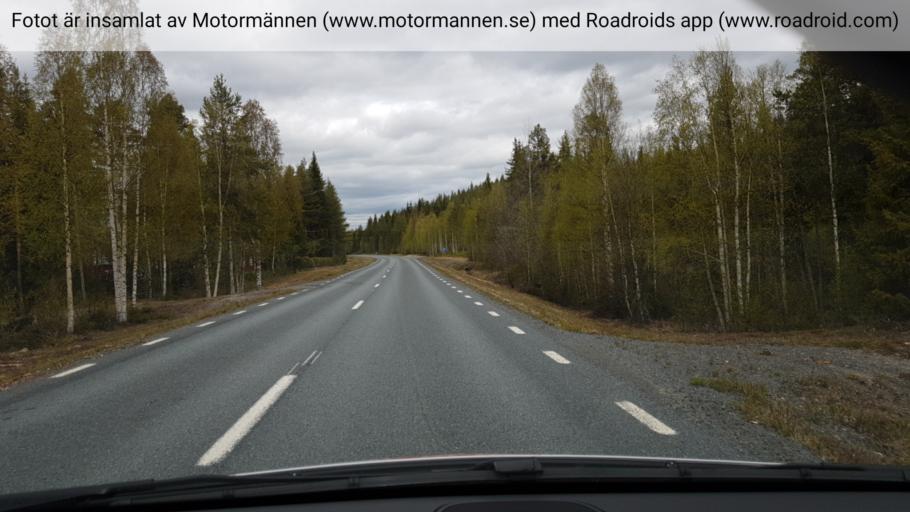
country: SE
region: Vaesterbotten
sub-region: Mala Kommun
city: Mala
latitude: 65.0649
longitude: 18.3716
